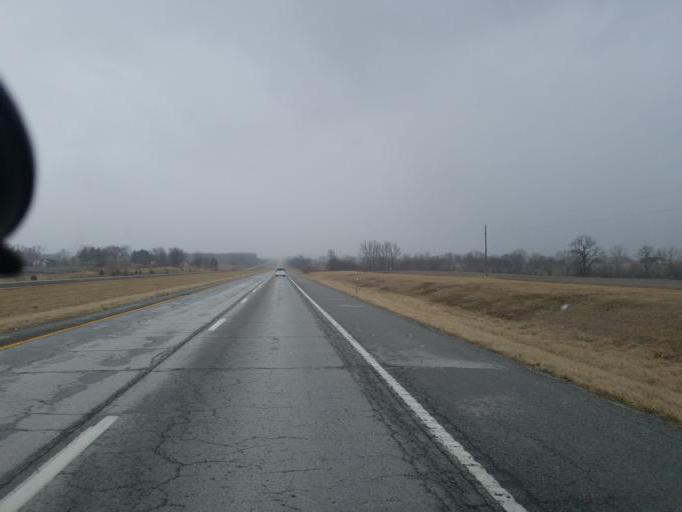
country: US
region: Missouri
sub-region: Macon County
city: La Plata
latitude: 40.0044
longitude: -92.4754
